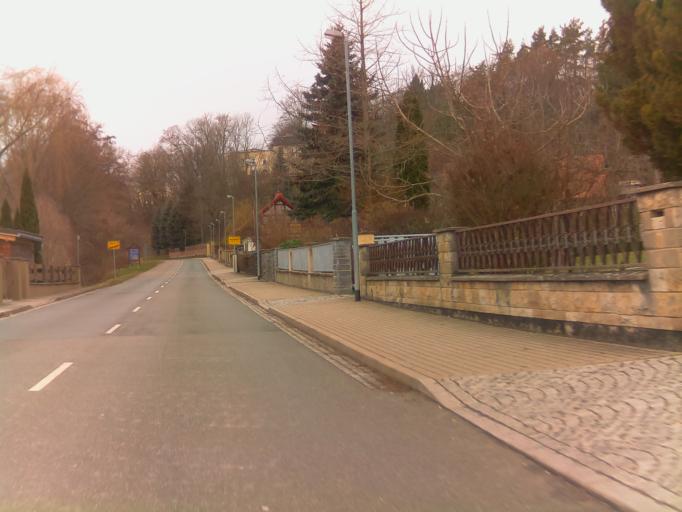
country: DE
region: Thuringia
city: Kraftsdorf
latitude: 50.8772
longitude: 11.9344
